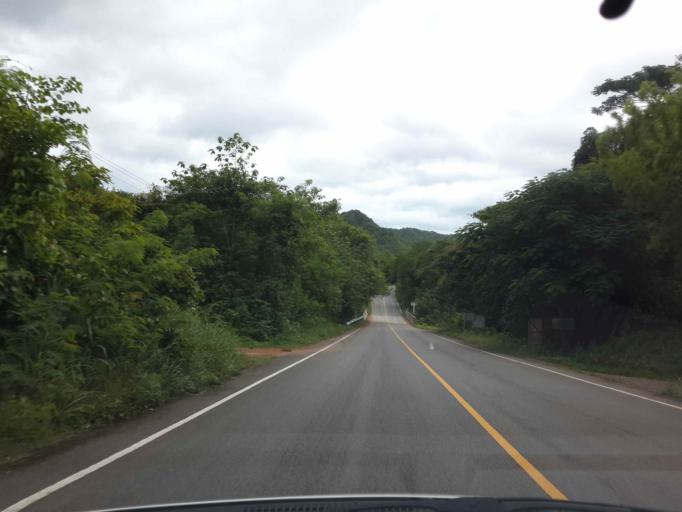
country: TH
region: Ratchaburi
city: Suan Phueng
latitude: 13.5698
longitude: 99.2544
